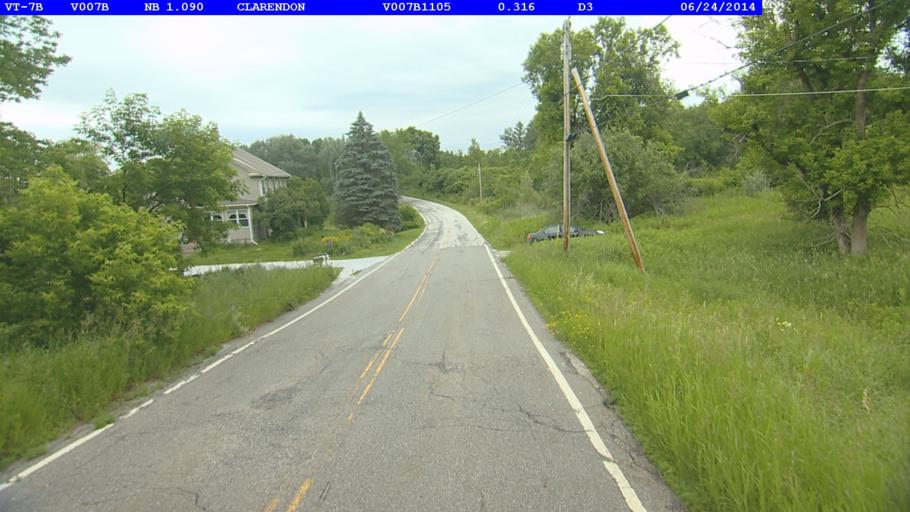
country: US
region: Vermont
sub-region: Rutland County
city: Rutland
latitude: 43.4999
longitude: -72.9707
